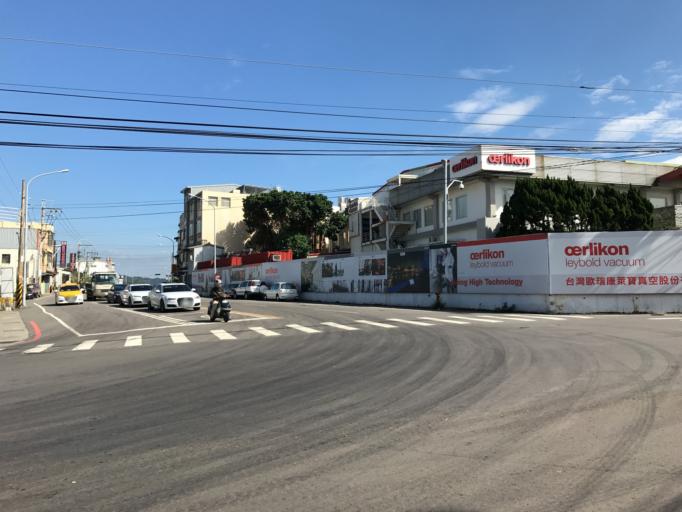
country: TW
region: Taiwan
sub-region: Hsinchu
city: Zhubei
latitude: 24.7713
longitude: 121.0510
